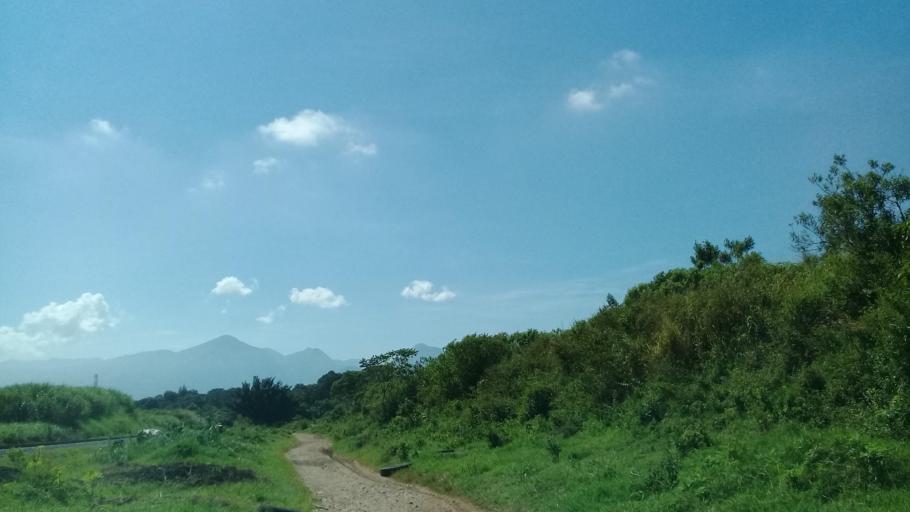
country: MX
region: Veracruz
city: Amatlan de los Reyes
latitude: 18.8593
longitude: -96.9206
